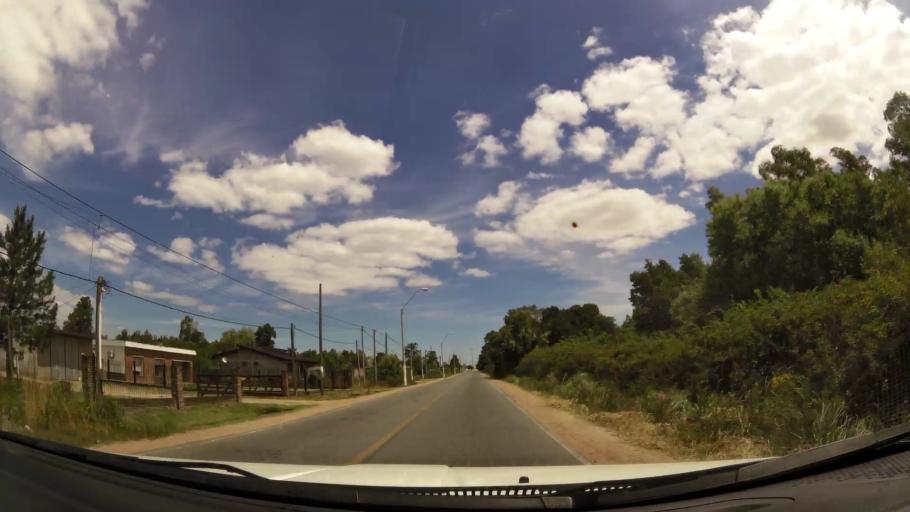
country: UY
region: San Jose
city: Delta del Tigre
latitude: -34.7362
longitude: -56.4471
